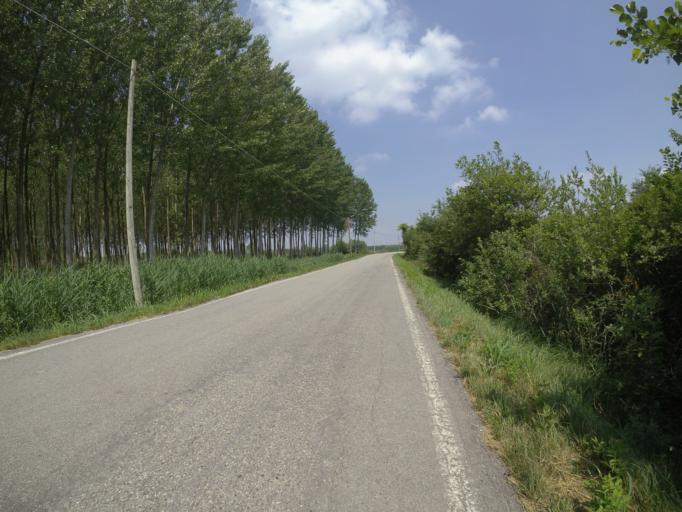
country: IT
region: Friuli Venezia Giulia
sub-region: Provincia di Udine
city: Bertiolo
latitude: 45.9111
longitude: 13.0474
